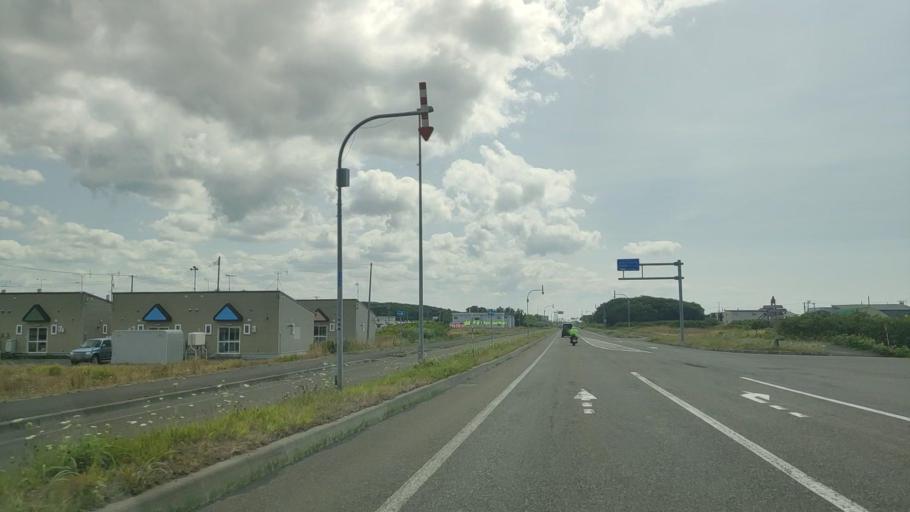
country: JP
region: Hokkaido
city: Makubetsu
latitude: 44.8809
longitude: 141.7497
